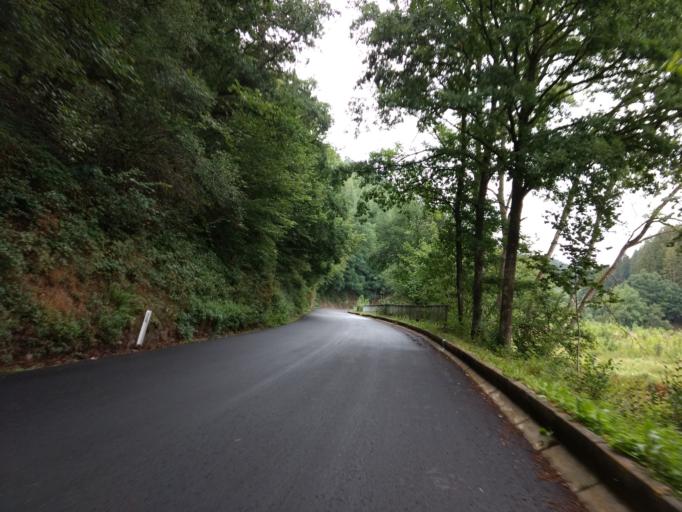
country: BE
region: Wallonia
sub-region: Province du Luxembourg
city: Houffalize
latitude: 50.1367
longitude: 5.7527
